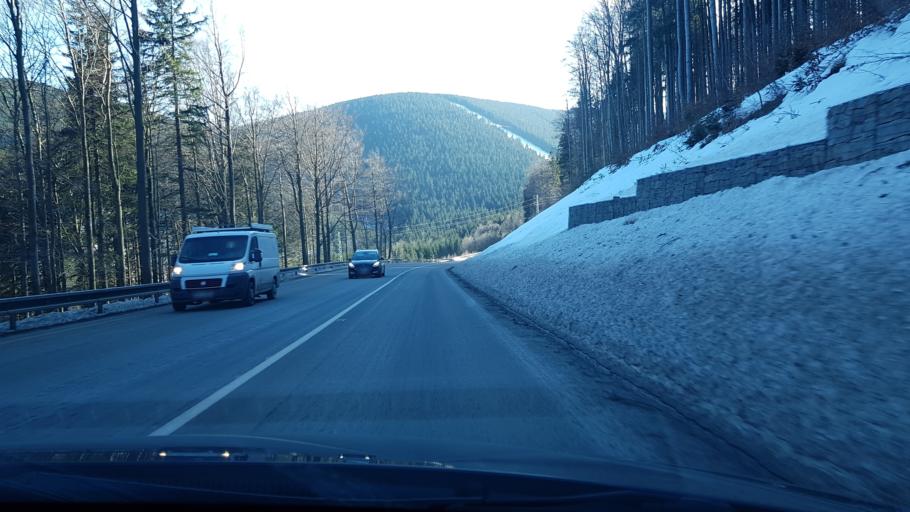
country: CZ
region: Olomoucky
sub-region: Okres Sumperk
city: Loucna nad Desnou
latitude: 50.1383
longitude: 17.1629
